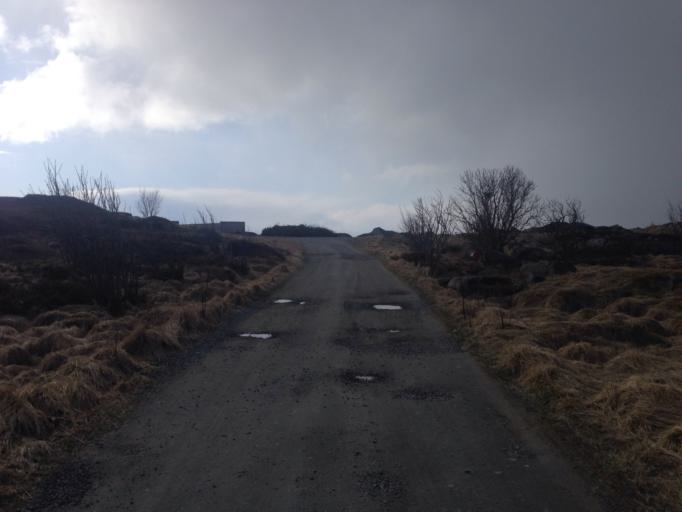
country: NO
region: Nordland
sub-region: Vagan
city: Kabelvag
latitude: 68.3858
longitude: 14.4090
